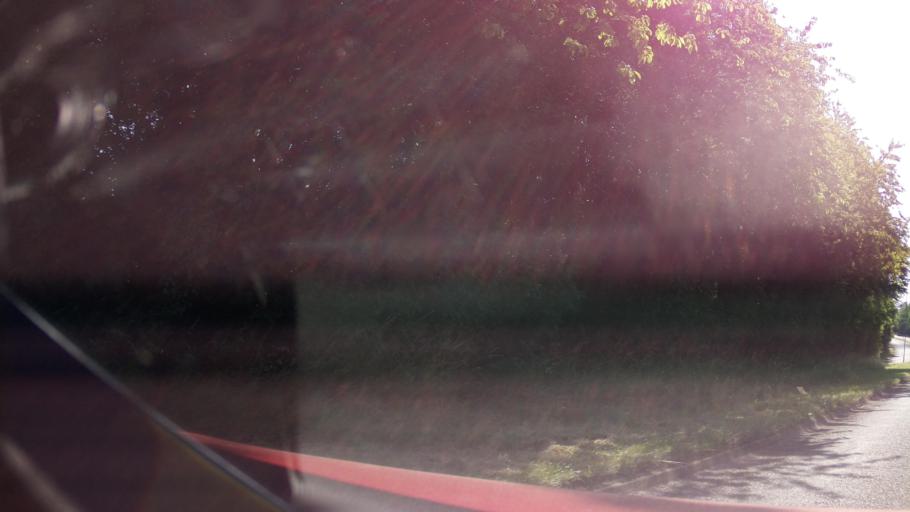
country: GB
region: England
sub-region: Worcestershire
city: Redditch
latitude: 52.2983
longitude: -1.9153
